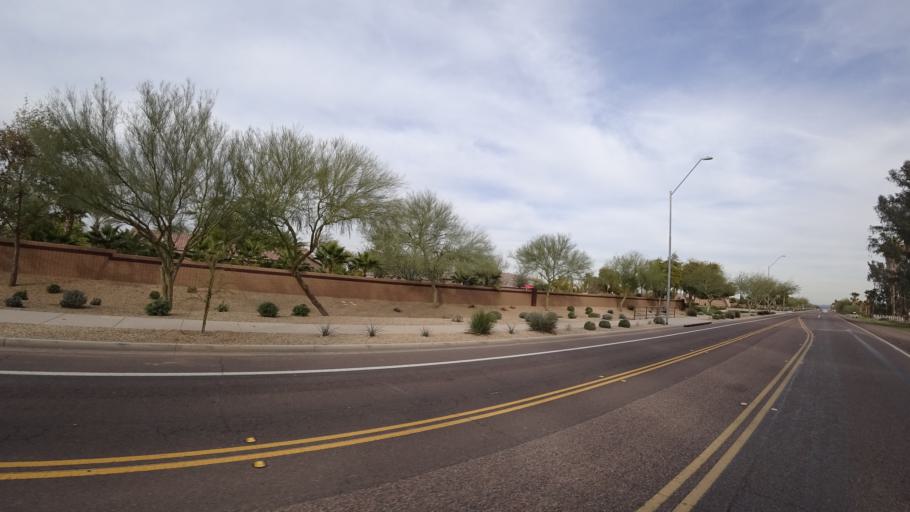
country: US
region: Arizona
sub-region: Maricopa County
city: El Mirage
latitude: 33.5803
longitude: -112.3693
